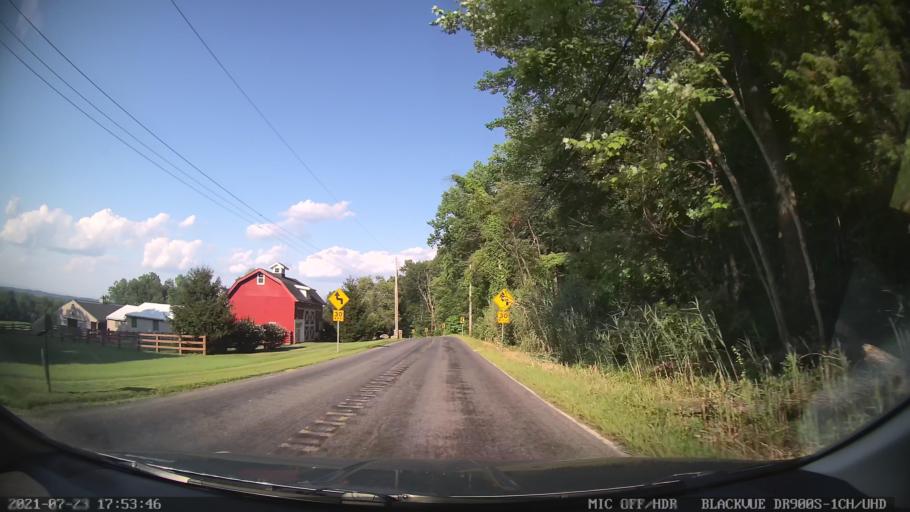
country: US
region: Pennsylvania
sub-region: Lehigh County
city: Macungie
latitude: 40.5054
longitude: -75.5611
